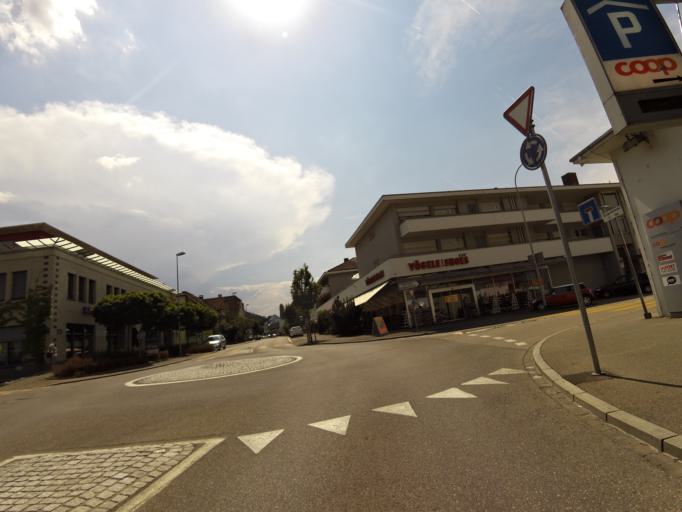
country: CH
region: Aargau
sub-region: Bezirk Lenzburg
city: Lenzburg
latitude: 47.3895
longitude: 8.1711
